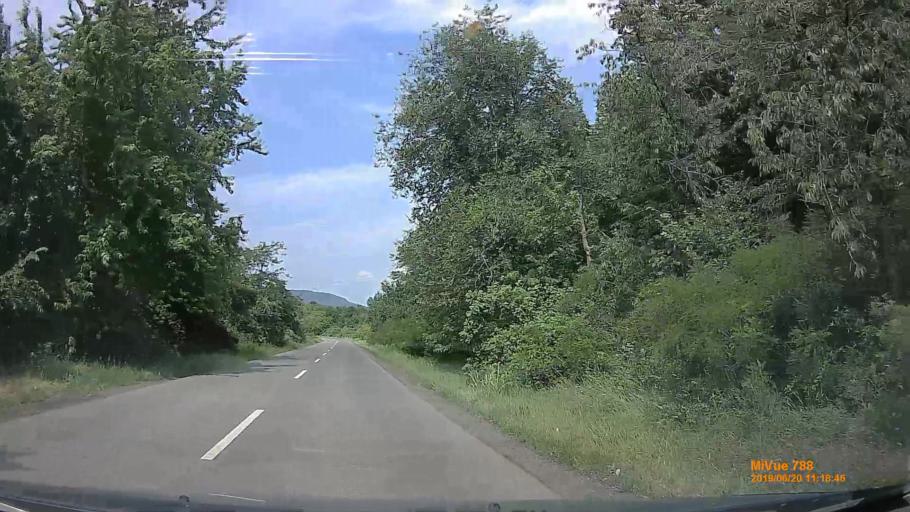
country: HU
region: Baranya
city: Pecsvarad
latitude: 46.1682
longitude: 18.4557
